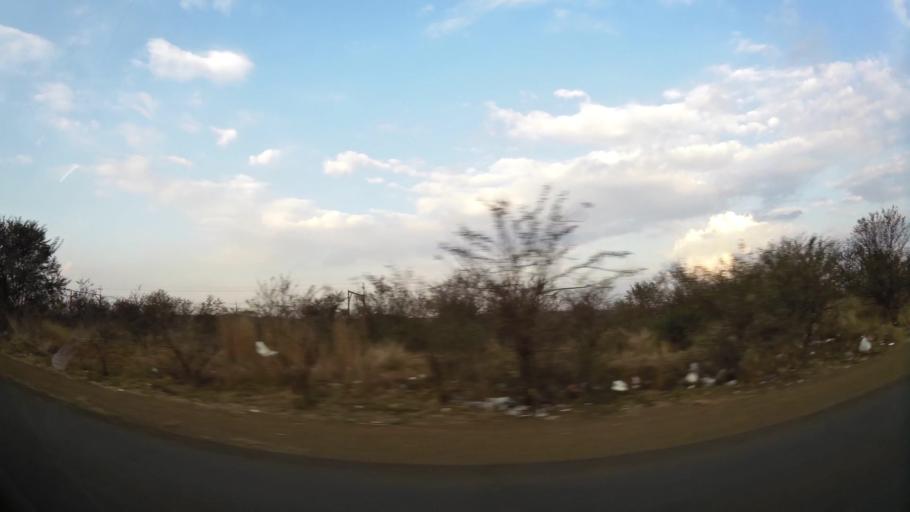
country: ZA
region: Gauteng
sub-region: City of Johannesburg Metropolitan Municipality
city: Orange Farm
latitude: -26.5854
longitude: 27.8543
